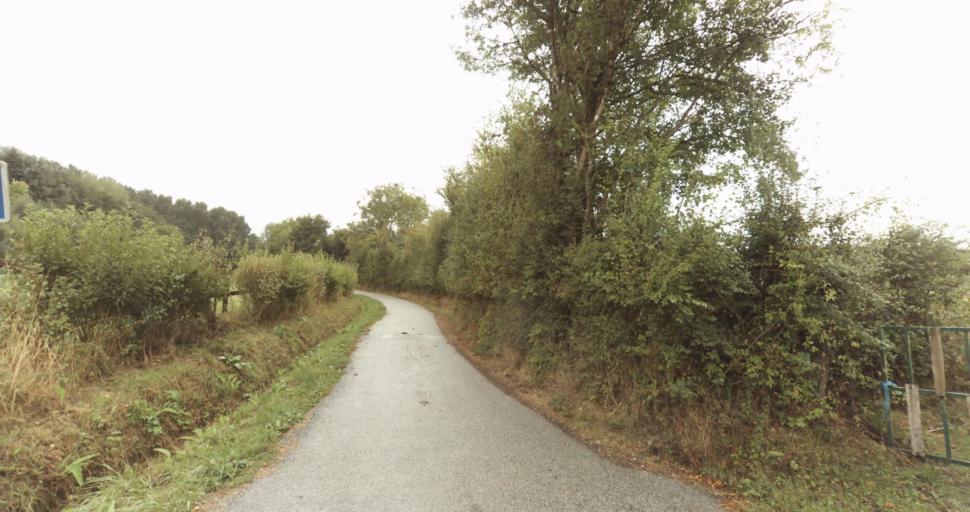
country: FR
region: Lower Normandy
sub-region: Departement de l'Orne
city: Sainte-Gauburge-Sainte-Colombe
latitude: 48.7108
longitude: 0.4308
